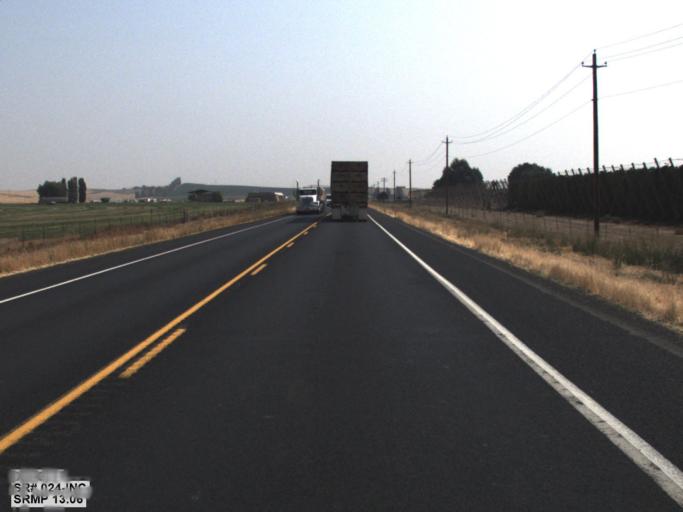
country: US
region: Washington
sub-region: Yakima County
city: Zillah
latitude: 46.5202
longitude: -120.2272
